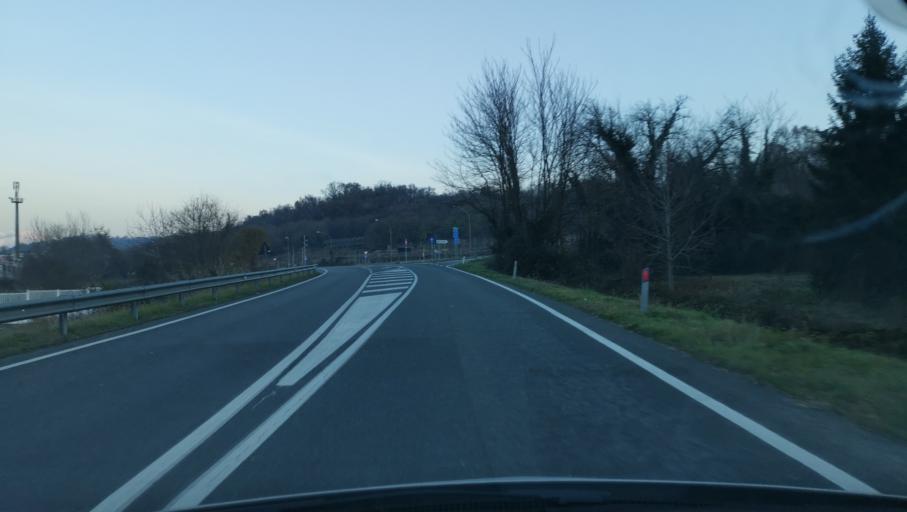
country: IT
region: Piedmont
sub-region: Provincia di Torino
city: Barone Canavese
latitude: 45.3141
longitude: 7.8801
